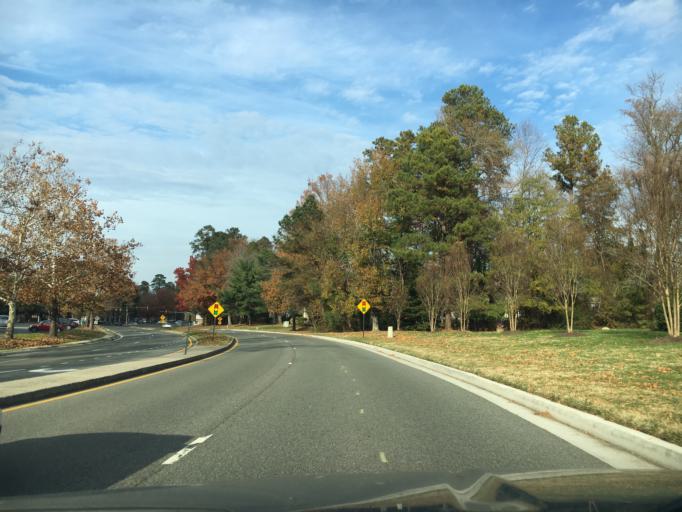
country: US
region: Virginia
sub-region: Henrico County
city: Tuckahoe
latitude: 37.6012
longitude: -77.5443
